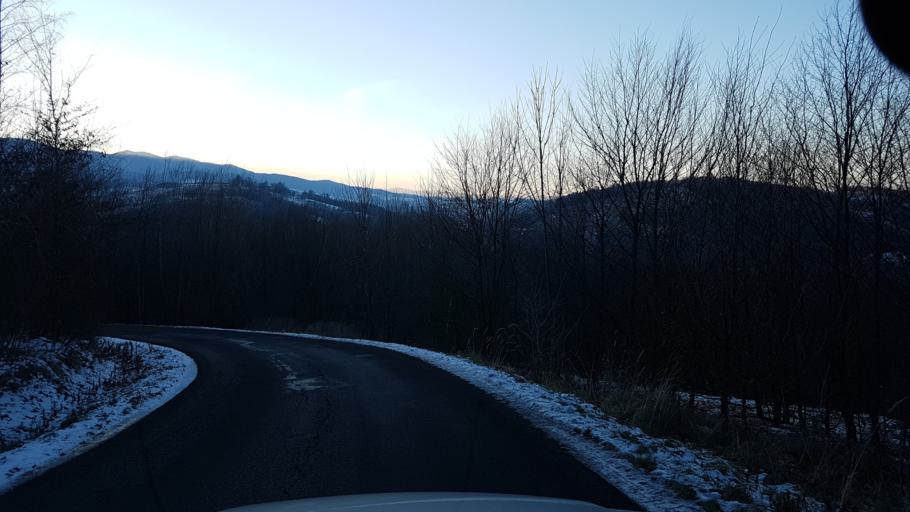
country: PL
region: Lesser Poland Voivodeship
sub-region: Powiat nowosadecki
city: Rytro
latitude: 49.5156
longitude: 20.6628
